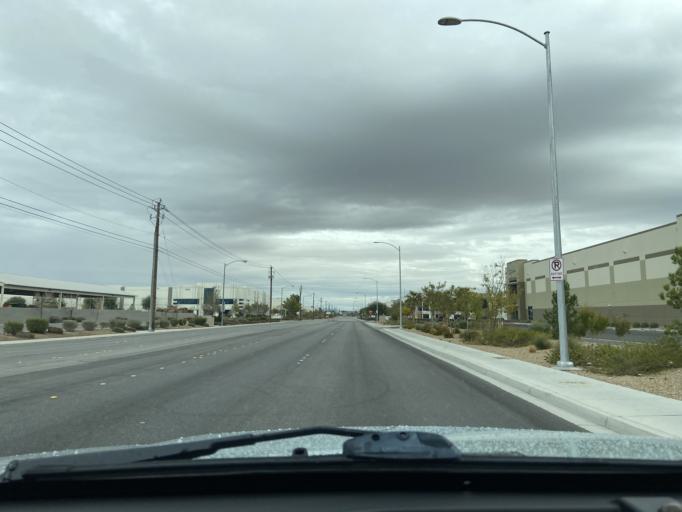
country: US
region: Nevada
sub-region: Clark County
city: North Las Vegas
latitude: 36.2469
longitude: -115.1097
